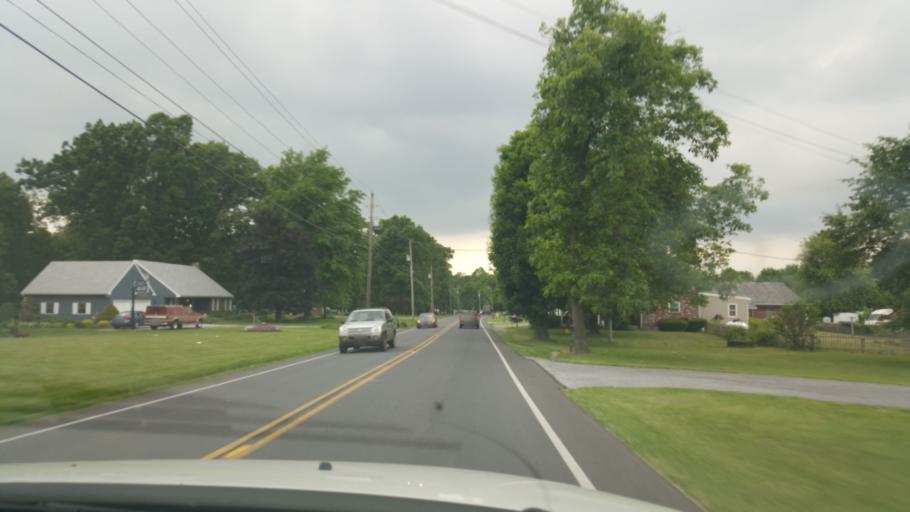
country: US
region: Pennsylvania
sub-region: Adams County
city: Lake Meade
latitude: 39.9496
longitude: -77.1080
